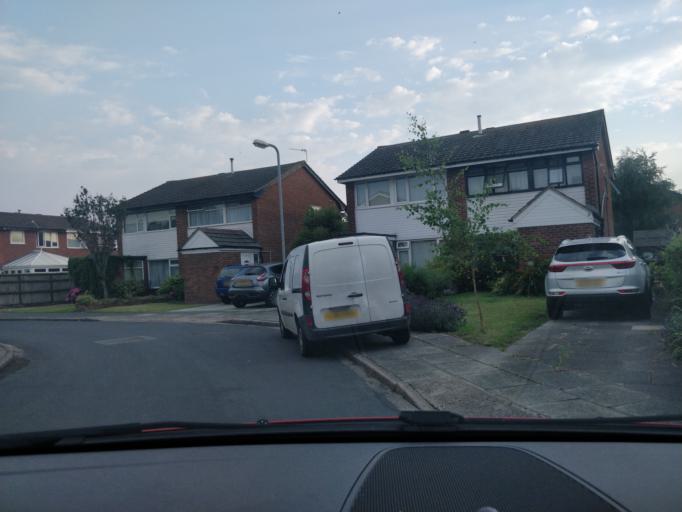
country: GB
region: England
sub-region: Sefton
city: Southport
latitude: 53.6728
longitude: -2.9734
